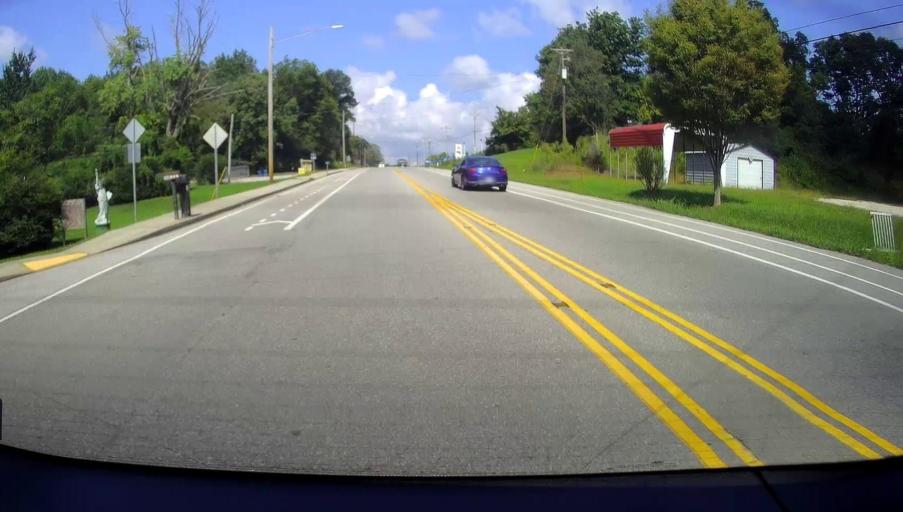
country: US
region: Tennessee
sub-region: Coffee County
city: Manchester
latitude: 35.4891
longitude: -86.0940
